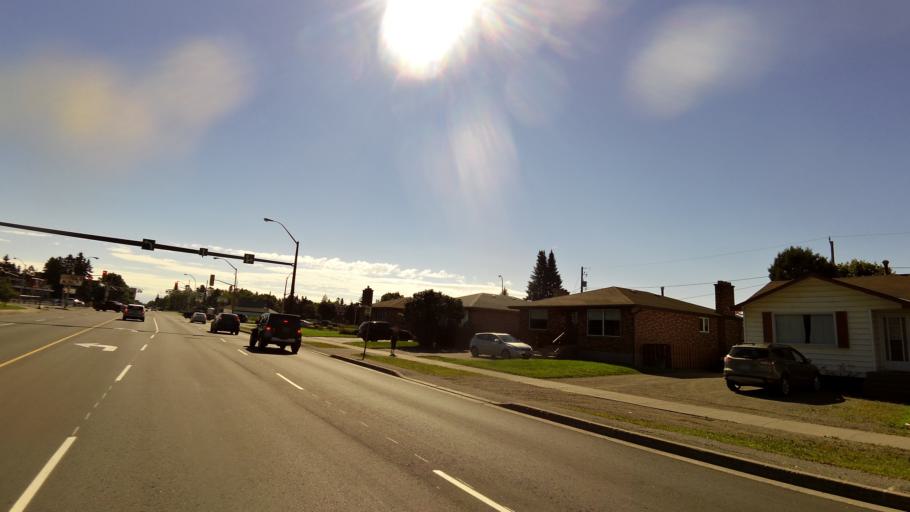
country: CA
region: Ontario
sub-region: Thunder Bay District
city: Thunder Bay
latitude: 48.3808
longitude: -89.2672
